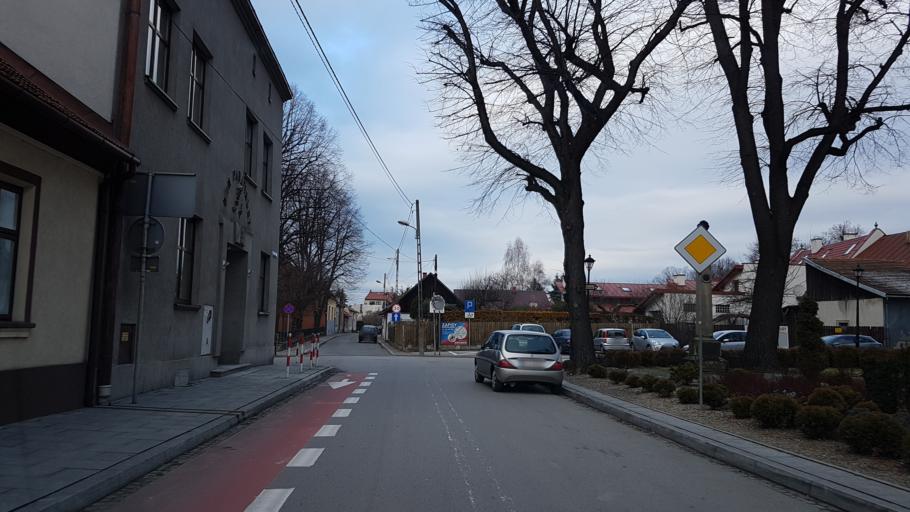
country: PL
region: Lesser Poland Voivodeship
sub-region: Powiat nowosadecki
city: Stary Sacz
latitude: 49.5612
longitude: 20.6351
